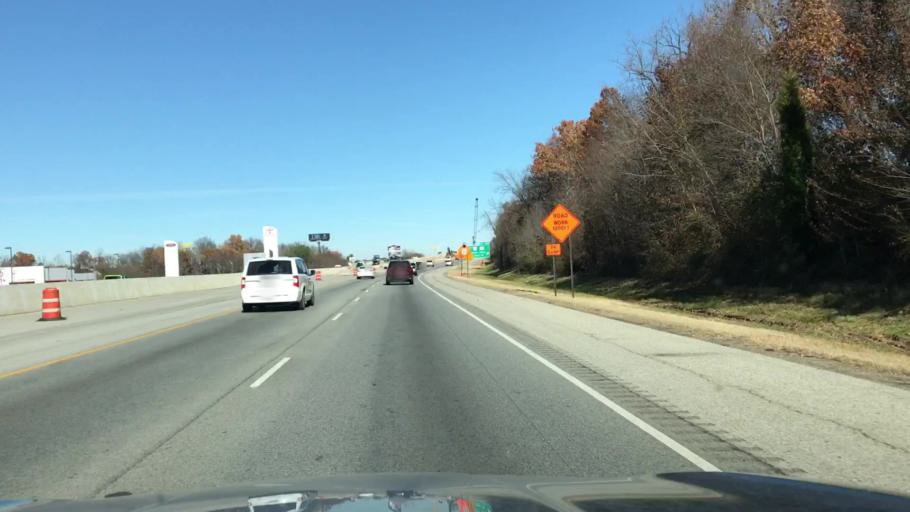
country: US
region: Arkansas
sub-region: Benton County
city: Bentonville
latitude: 36.3294
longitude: -94.1845
